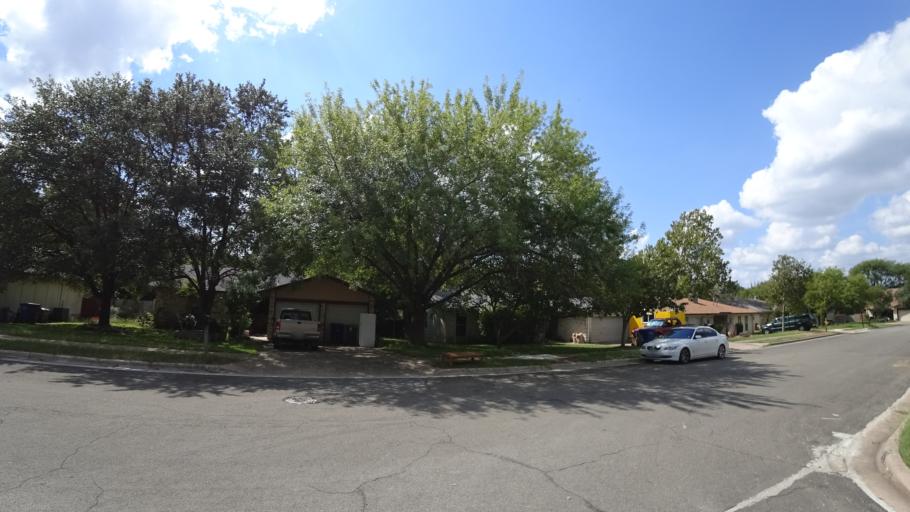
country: US
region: Texas
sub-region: Travis County
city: Onion Creek
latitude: 30.1901
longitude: -97.7866
